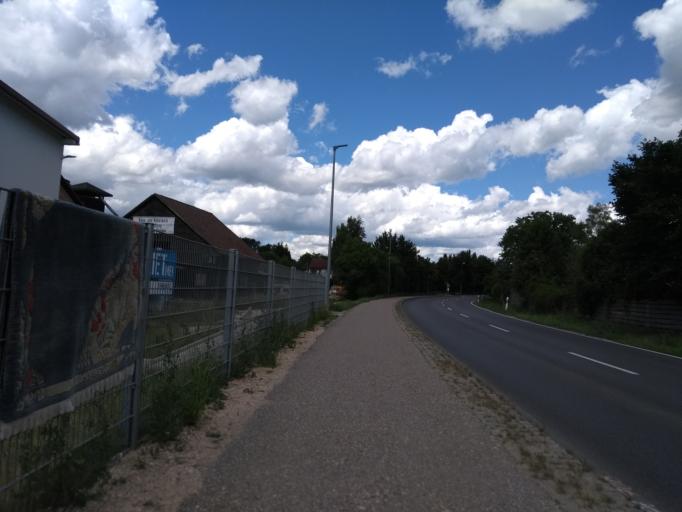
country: DE
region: Baden-Wuerttemberg
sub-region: Tuebingen Region
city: Ehingen
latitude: 48.2786
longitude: 9.7164
